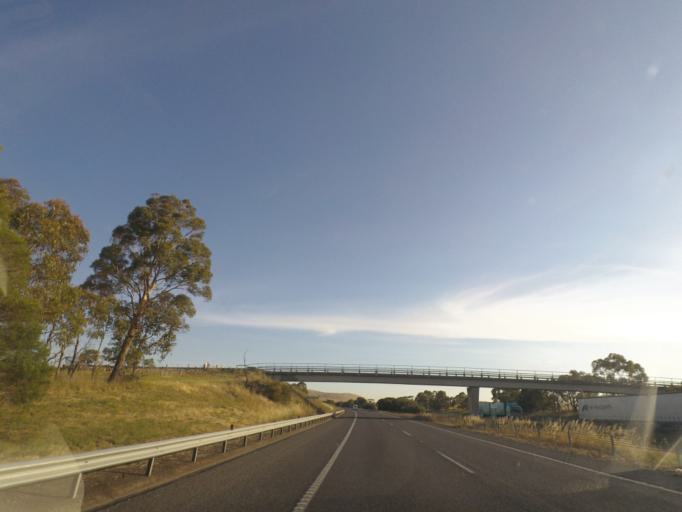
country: AU
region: Victoria
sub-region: Whittlesea
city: Whittlesea
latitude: -37.4346
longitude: 144.9821
